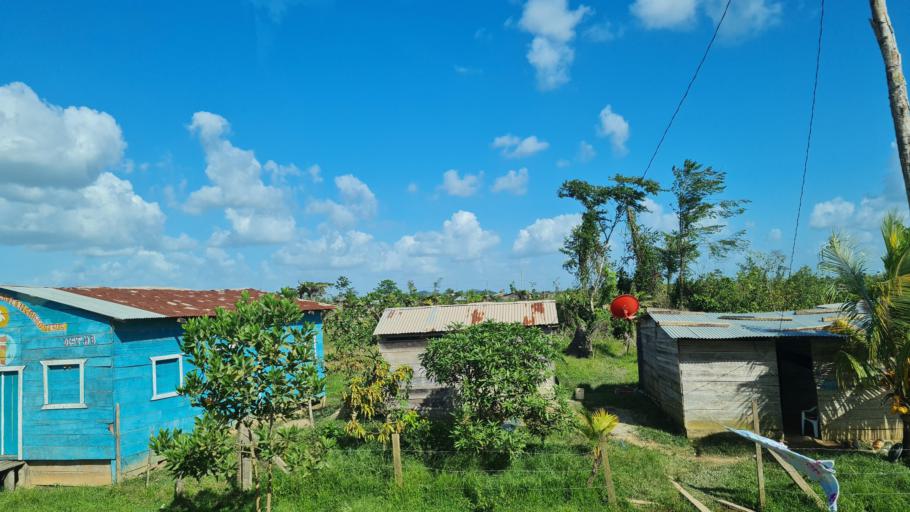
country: NI
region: Atlantico Norte (RAAN)
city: Bonanza
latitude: 13.9832
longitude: -84.1883
